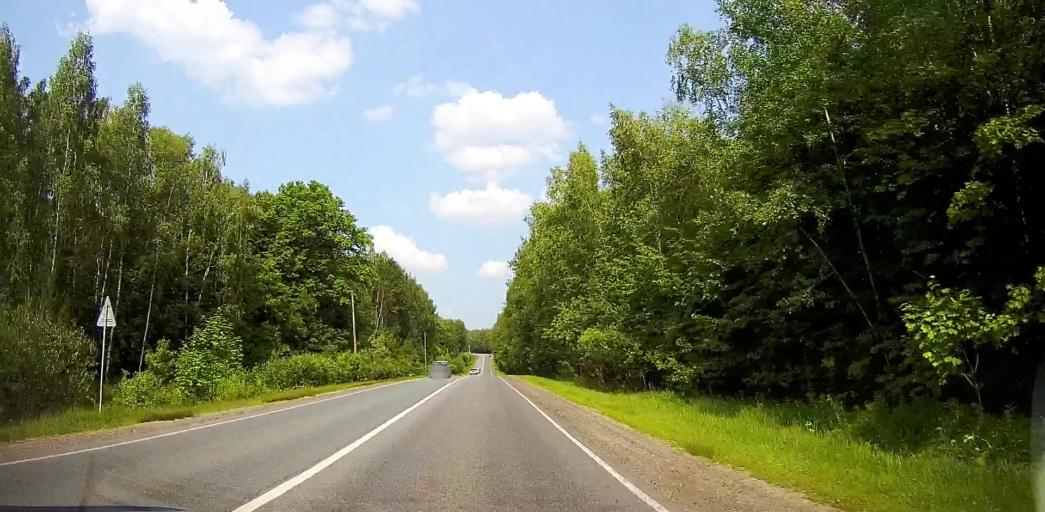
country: RU
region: Moskovskaya
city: Stupino
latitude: 54.9770
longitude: 38.1595
